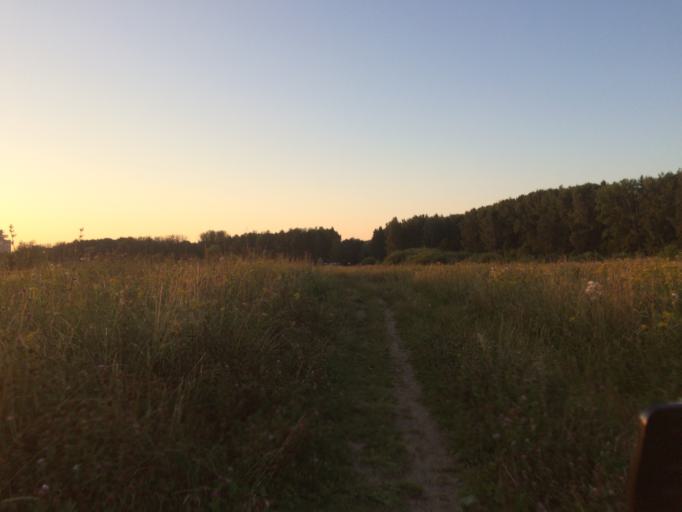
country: RU
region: Mariy-El
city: Yoshkar-Ola
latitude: 56.6197
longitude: 47.9170
